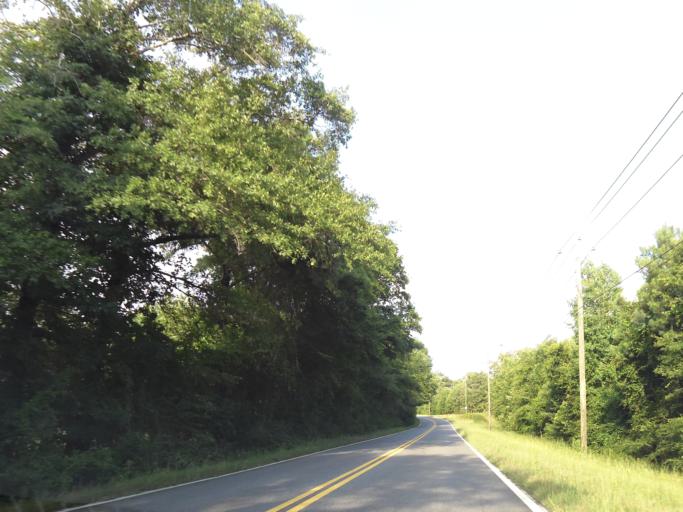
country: US
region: Georgia
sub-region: Houston County
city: Centerville
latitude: 32.7123
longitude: -83.6541
